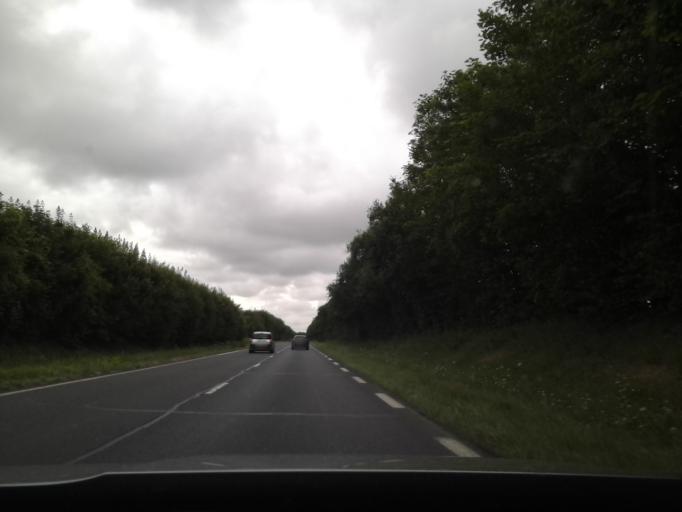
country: FR
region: Lower Normandy
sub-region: Departement du Calvados
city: Le Molay-Littry
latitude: 49.3307
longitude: -0.8938
